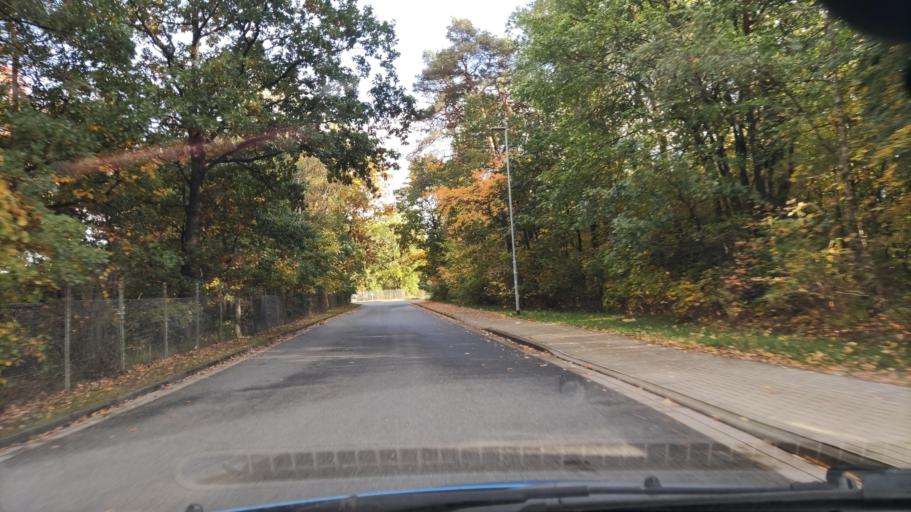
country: DE
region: Lower Saxony
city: Munster
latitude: 52.9749
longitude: 10.0814
